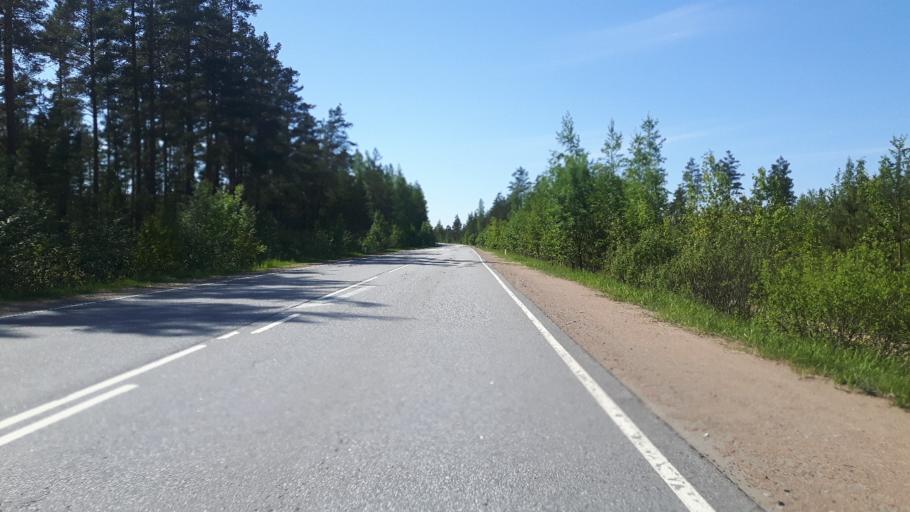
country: RU
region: Leningrad
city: Sista-Palkino
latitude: 59.7686
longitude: 28.7950
